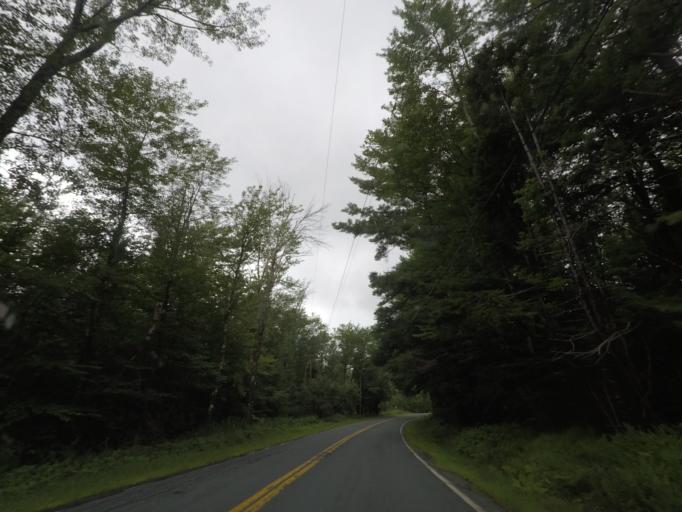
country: US
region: New York
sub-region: Rensselaer County
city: Poestenkill
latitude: 42.6895
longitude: -73.4479
